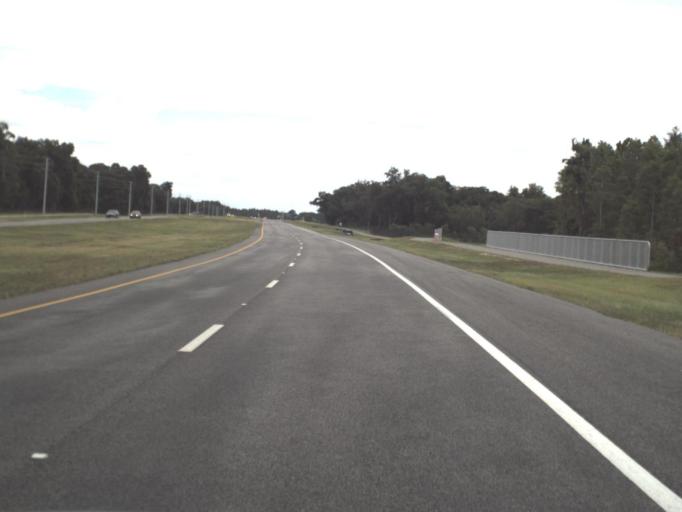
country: US
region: Florida
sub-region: Pasco County
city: Wesley Chapel
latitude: 28.1977
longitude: -82.3097
